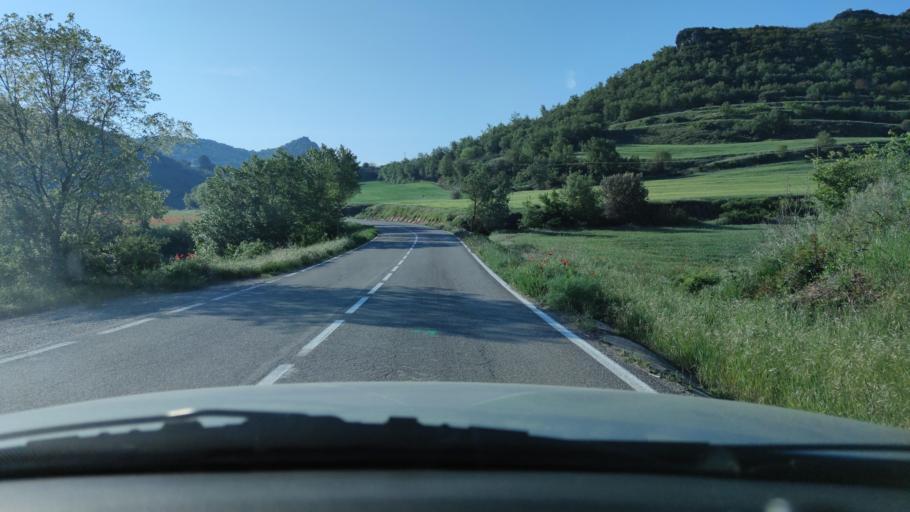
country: ES
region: Catalonia
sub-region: Provincia de Lleida
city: Cubells
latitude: 41.8872
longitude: 0.9940
